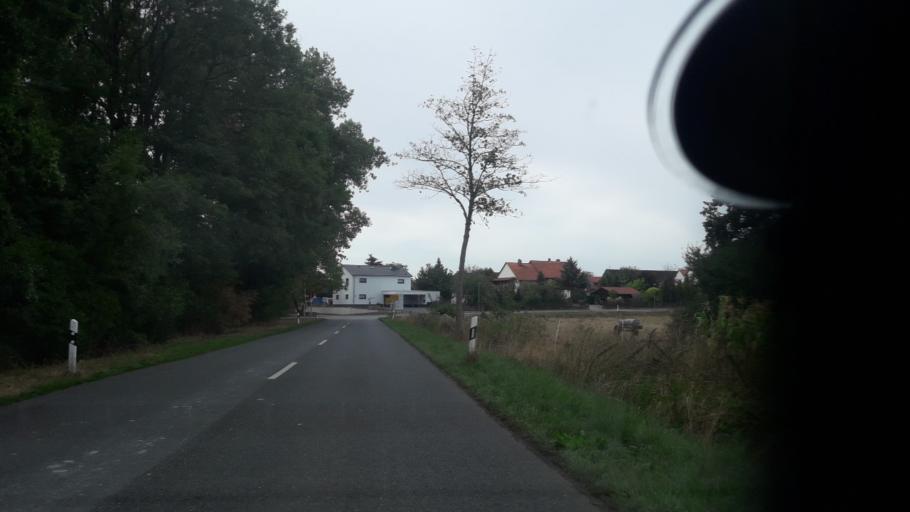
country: DE
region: Lower Saxony
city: Gross Twulpstedt
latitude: 52.3468
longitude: 10.8597
